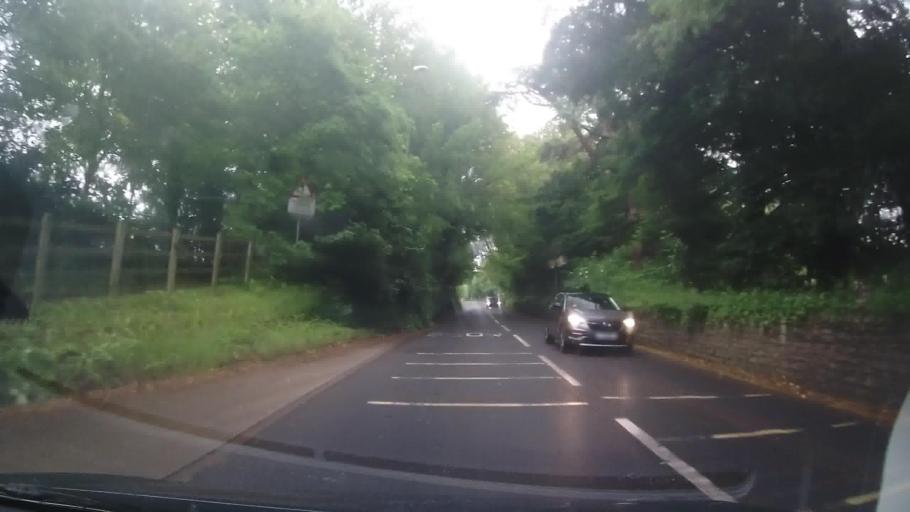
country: GB
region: England
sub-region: Borough of Torbay
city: Brixham
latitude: 50.3912
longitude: -3.5465
